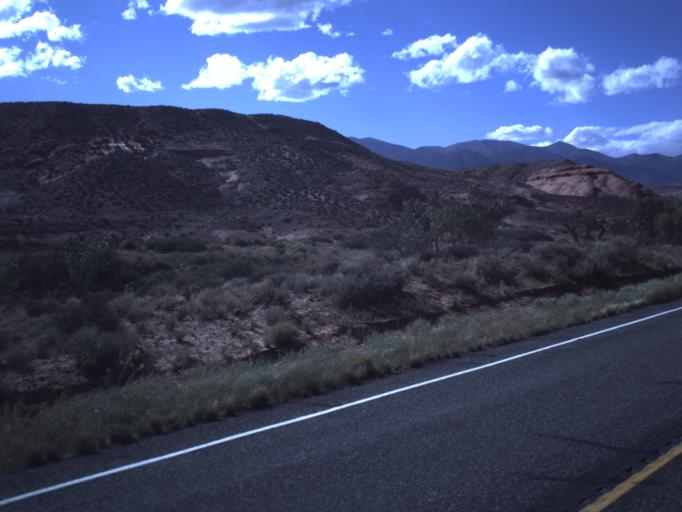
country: US
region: Utah
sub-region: Wayne County
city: Loa
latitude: 38.0557
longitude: -110.5907
